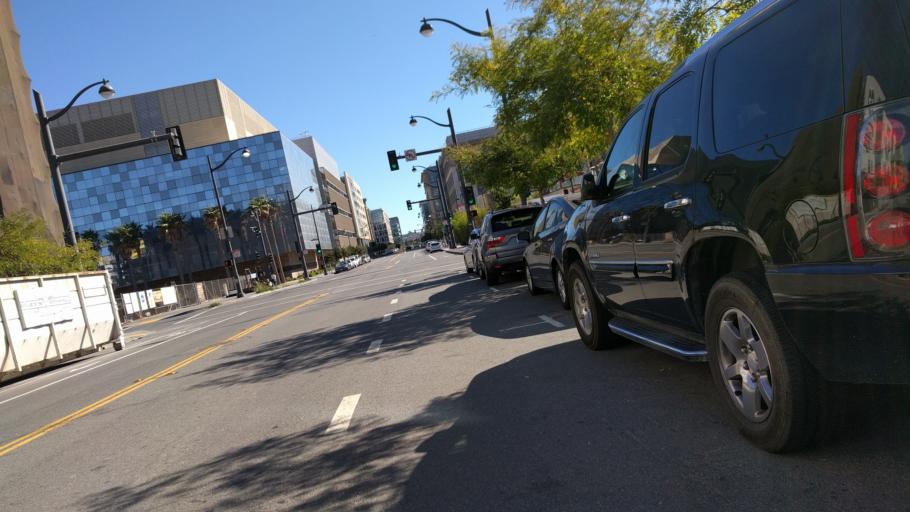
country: US
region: California
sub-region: San Francisco County
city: San Francisco
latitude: 37.7713
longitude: -122.3912
